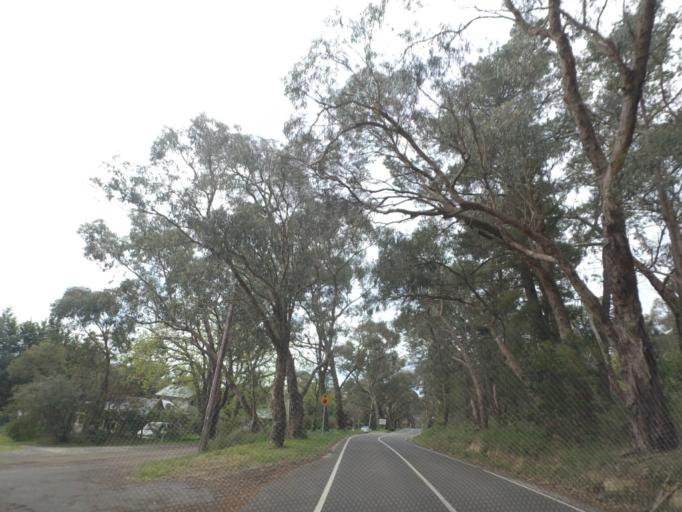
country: AU
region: Victoria
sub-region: Yarra Ranges
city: Montrose
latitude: -37.8159
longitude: 145.3502
